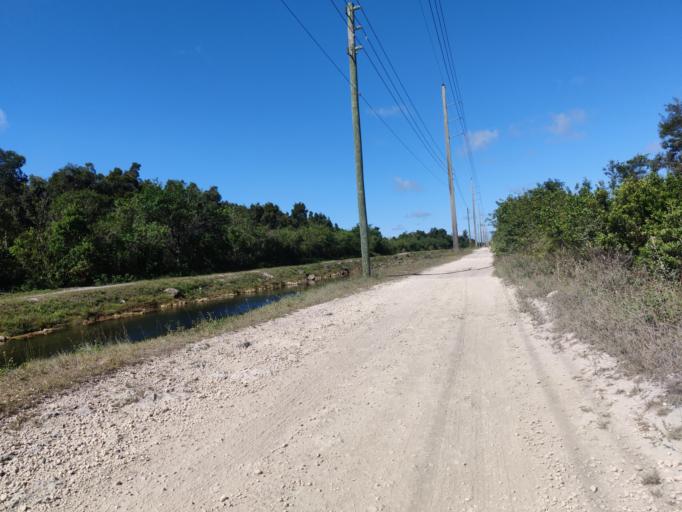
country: US
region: Florida
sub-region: Miami-Dade County
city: Kendall West
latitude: 25.7275
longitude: -80.4644
